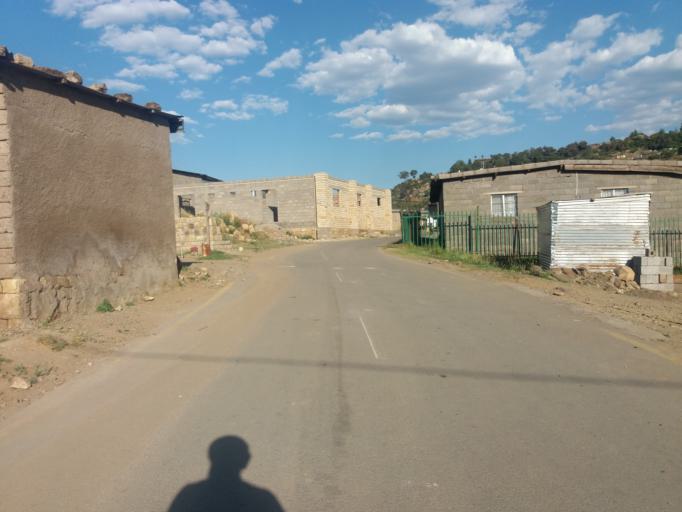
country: LS
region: Quthing
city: Quthing
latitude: -30.3993
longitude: 27.6990
